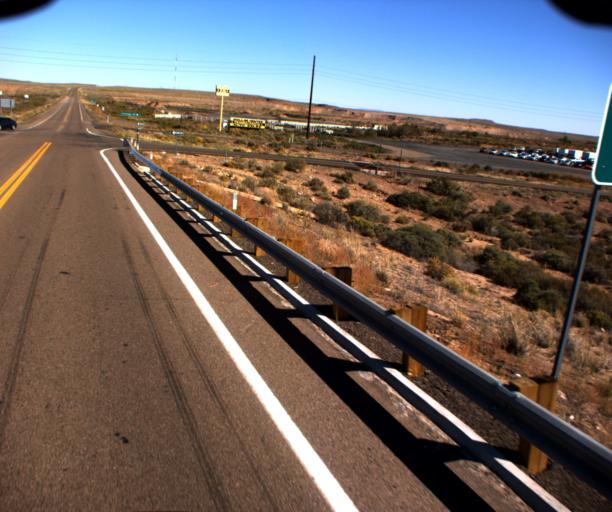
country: US
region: Arizona
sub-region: Navajo County
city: Winslow
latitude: 35.0101
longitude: -110.6407
